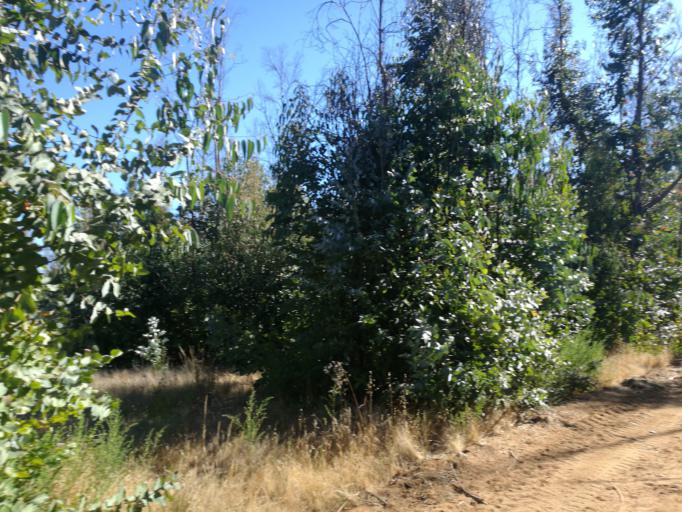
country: CL
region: Valparaiso
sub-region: Provincia de Valparaiso
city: Valparaiso
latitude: -33.0695
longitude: -71.6485
